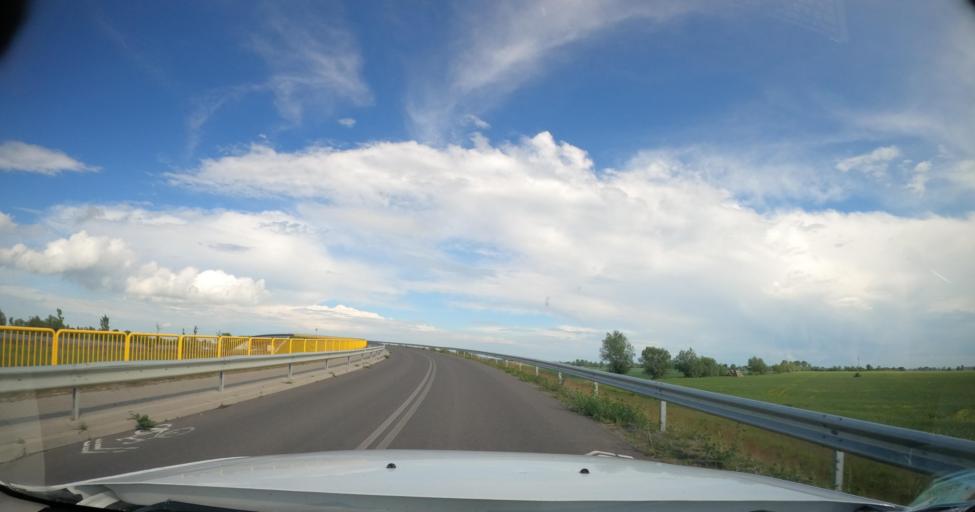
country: PL
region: Pomeranian Voivodeship
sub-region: Powiat nowodworski
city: Nowy Dwor Gdanski
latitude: 54.1881
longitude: 19.1671
